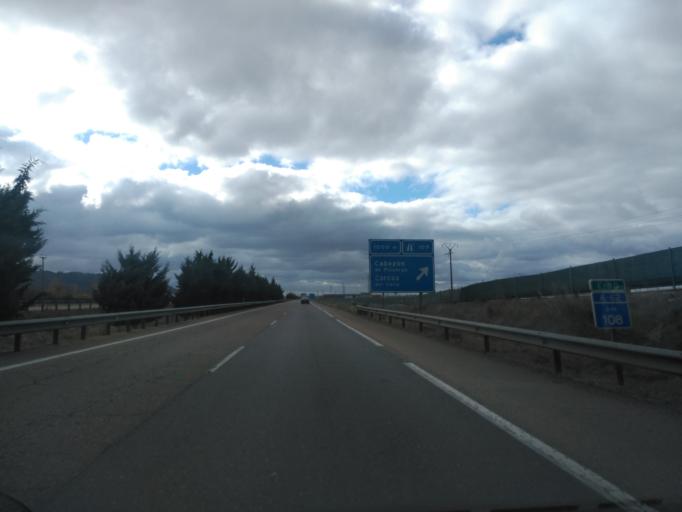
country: ES
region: Castille and Leon
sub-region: Provincia de Valladolid
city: Cabezon
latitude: 41.7678
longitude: -4.6252
